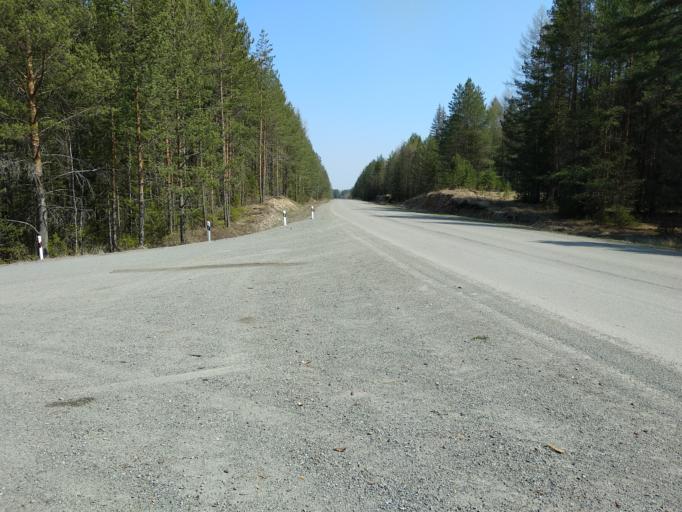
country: RU
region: Sverdlovsk
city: Karpinsk
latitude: 59.7298
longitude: 59.9527
